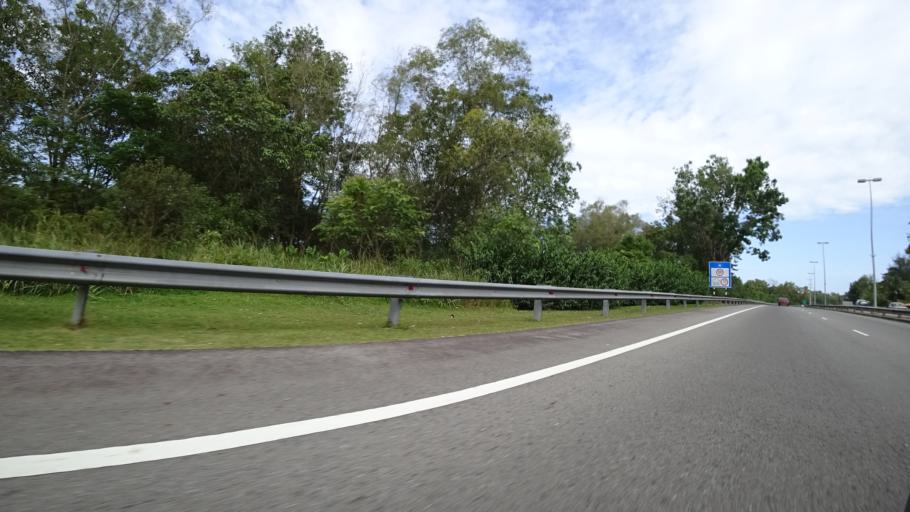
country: BN
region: Brunei and Muara
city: Bandar Seri Begawan
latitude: 4.9336
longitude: 114.9117
